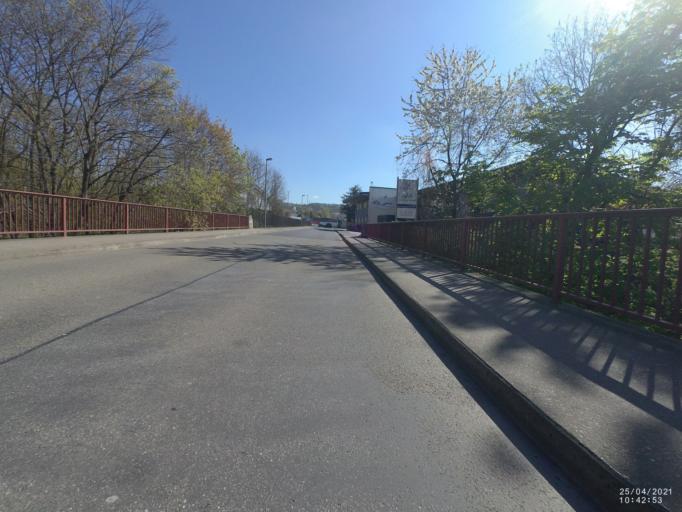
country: DE
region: Rheinland-Pfalz
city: Sankt Sebastian
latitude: 50.4269
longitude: 7.5631
